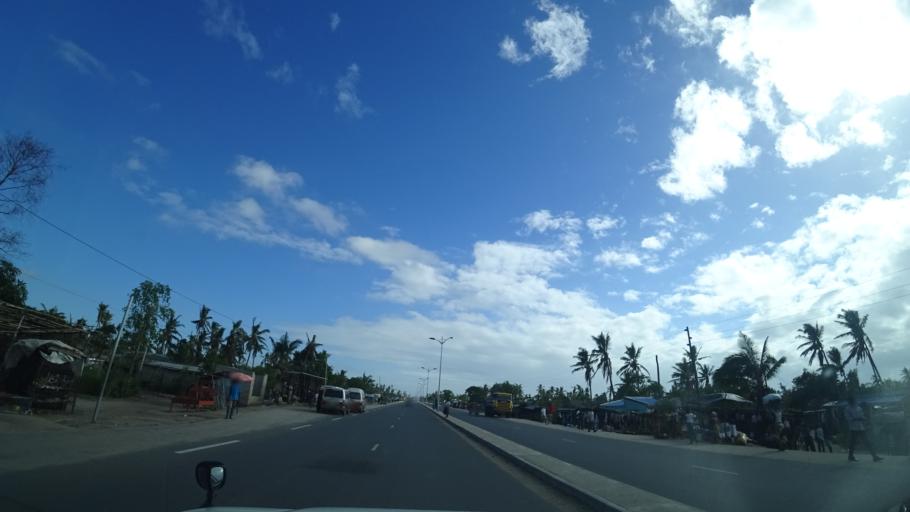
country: MZ
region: Sofala
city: Beira
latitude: -19.7649
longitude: 34.8808
